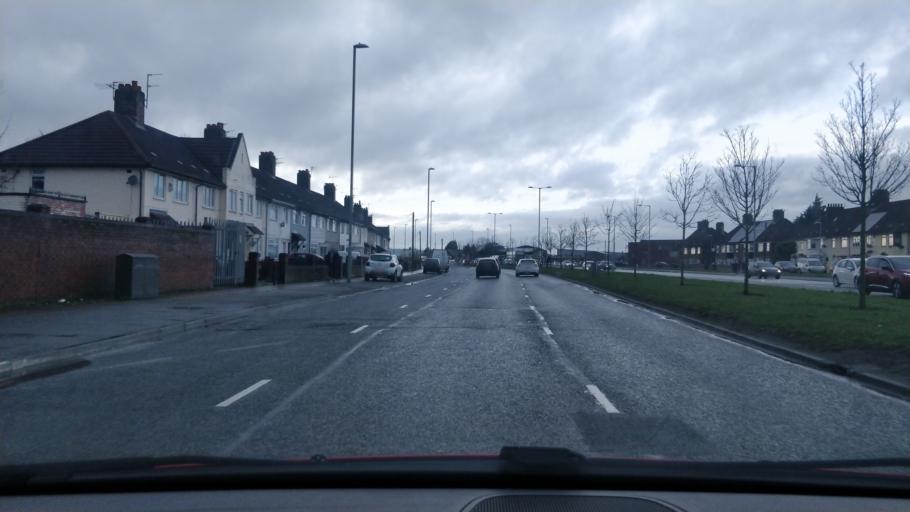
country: GB
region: England
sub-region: Knowsley
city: Huyton
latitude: 53.4208
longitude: -2.8559
